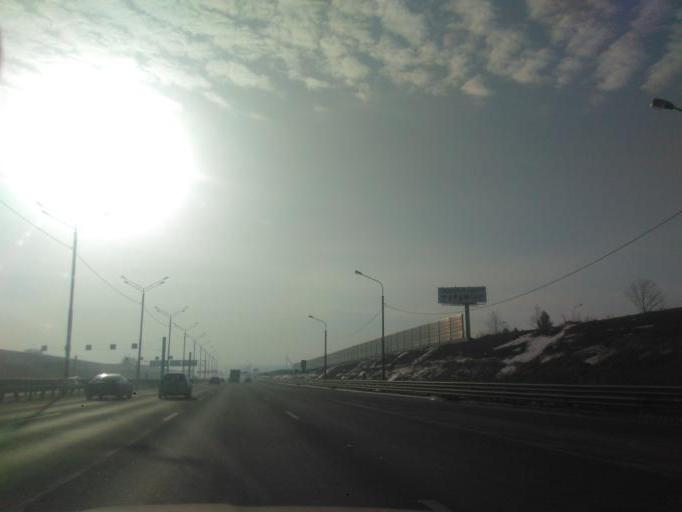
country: RU
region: Moskovskaya
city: Rozhdestveno
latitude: 55.8082
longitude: 37.0329
